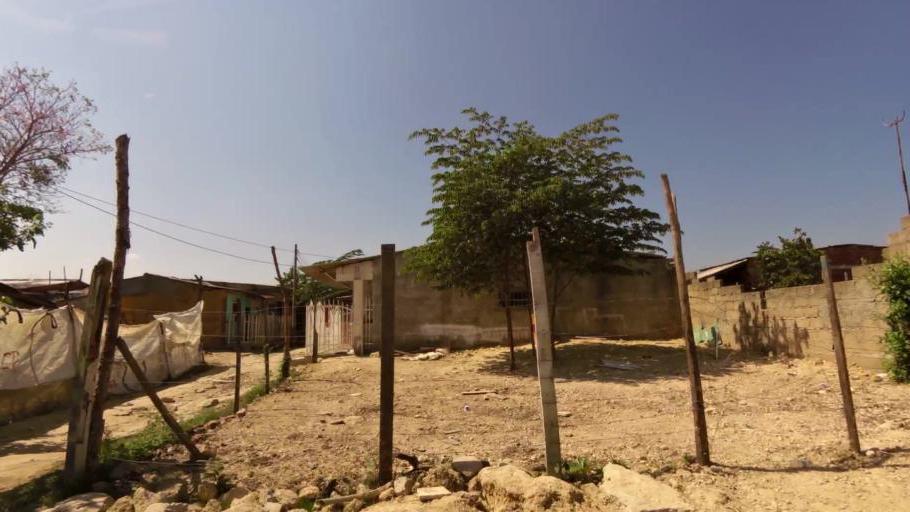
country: CO
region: Bolivar
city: Cartagena
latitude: 10.3542
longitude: -75.4857
